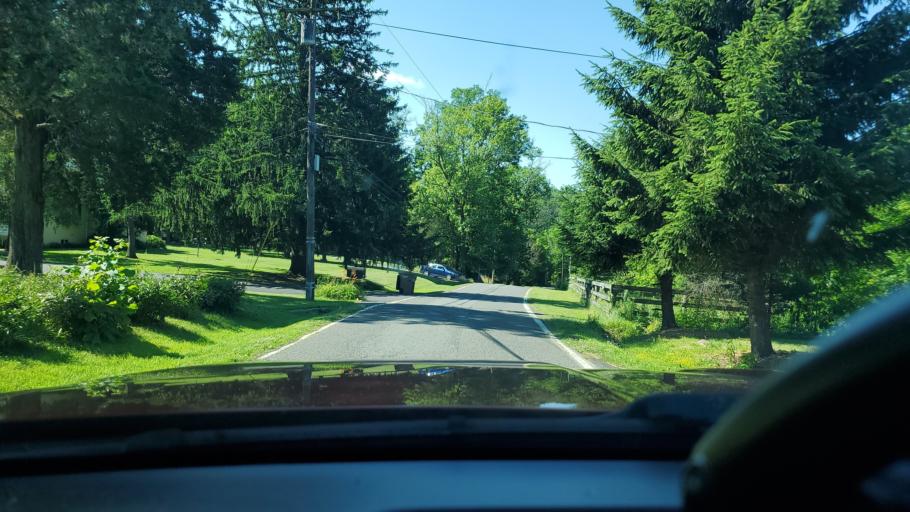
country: US
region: Pennsylvania
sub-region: Montgomery County
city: Red Hill
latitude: 40.3408
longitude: -75.5152
